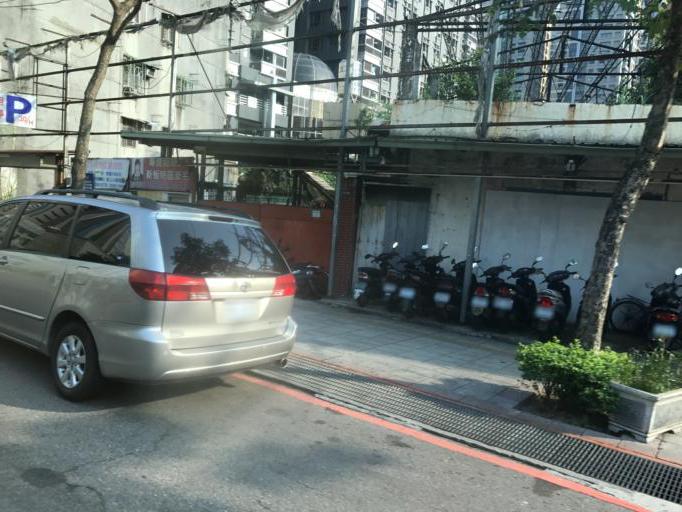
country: TW
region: Taipei
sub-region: Taipei
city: Banqiao
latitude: 25.0102
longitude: 121.4655
